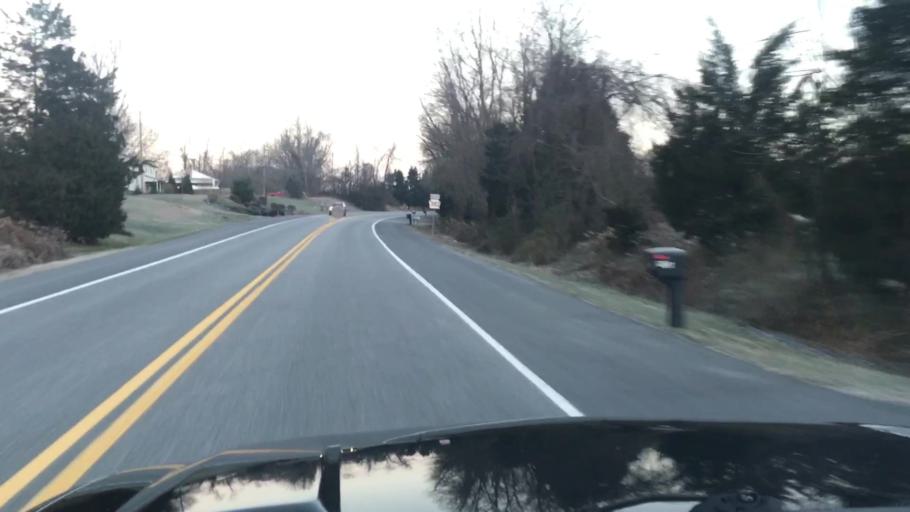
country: US
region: Pennsylvania
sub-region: Cumberland County
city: Lower Allen
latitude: 40.1589
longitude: -76.8856
